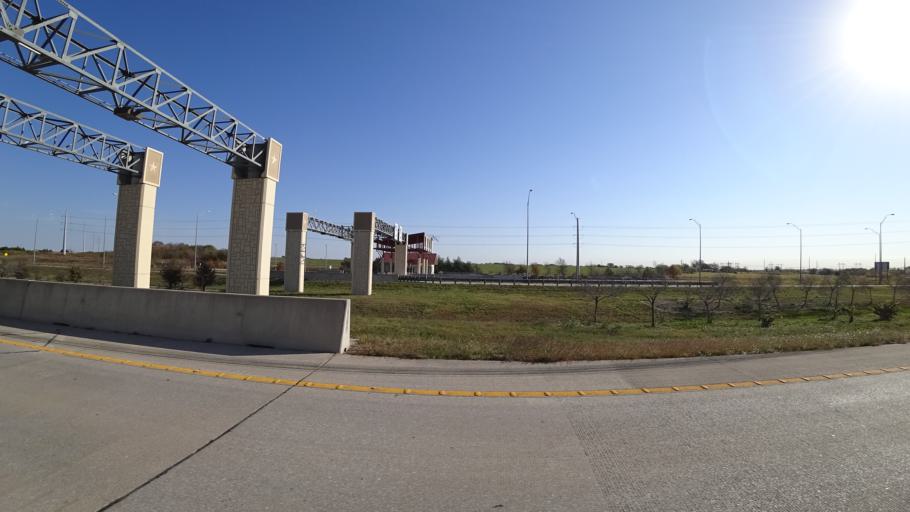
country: US
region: Texas
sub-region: Travis County
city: Pflugerville
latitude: 30.4143
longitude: -97.5858
